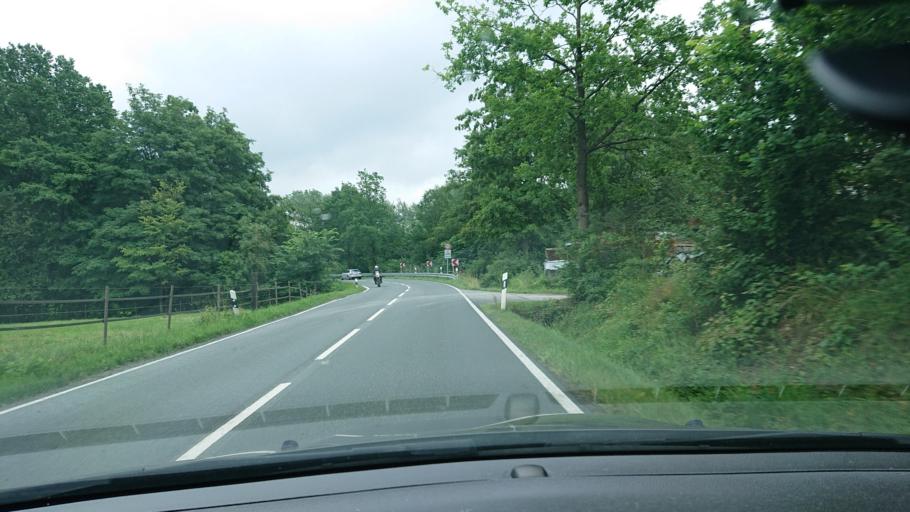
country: DE
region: North Rhine-Westphalia
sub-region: Regierungsbezirk Arnsberg
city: Mohnesee
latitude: 51.4717
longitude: 8.2327
